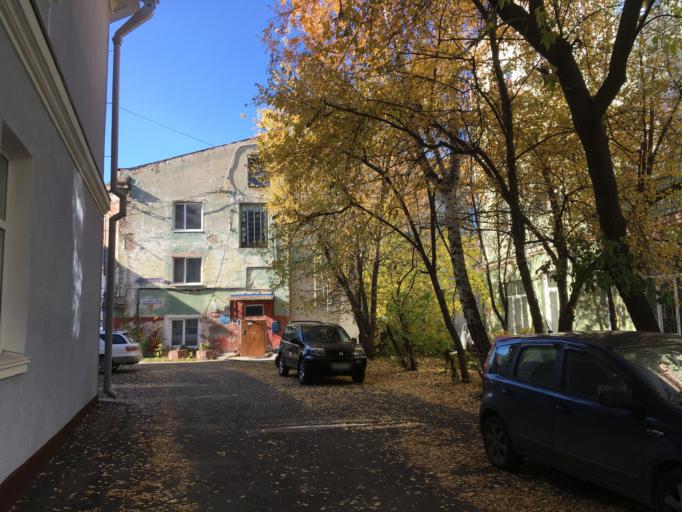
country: RU
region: Tomsk
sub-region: Tomskiy Rayon
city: Tomsk
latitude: 56.4945
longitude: 84.9501
